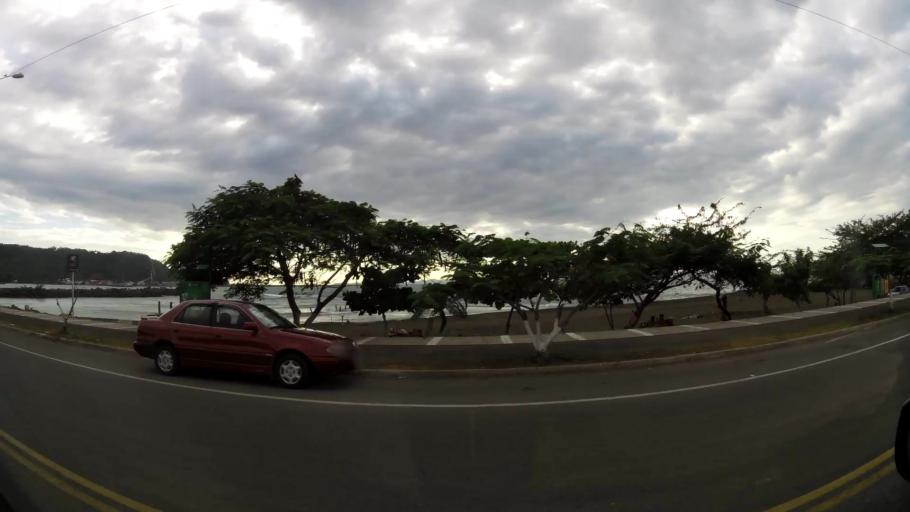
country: CR
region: Puntarenas
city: Esparza
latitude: 9.9235
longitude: -84.7138
